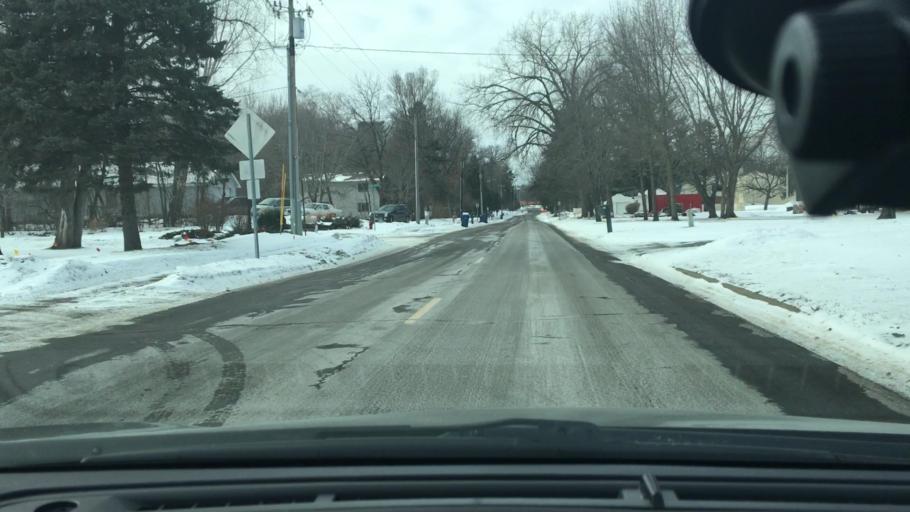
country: US
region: Minnesota
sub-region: Hennepin County
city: Champlin
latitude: 45.1854
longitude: -93.3937
